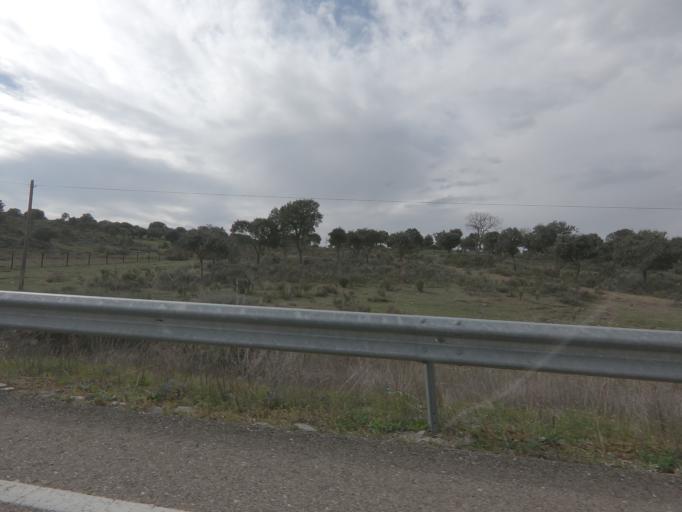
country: ES
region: Castille and Leon
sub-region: Provincia de Salamanca
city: Robleda
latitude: 40.4454
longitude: -6.5985
